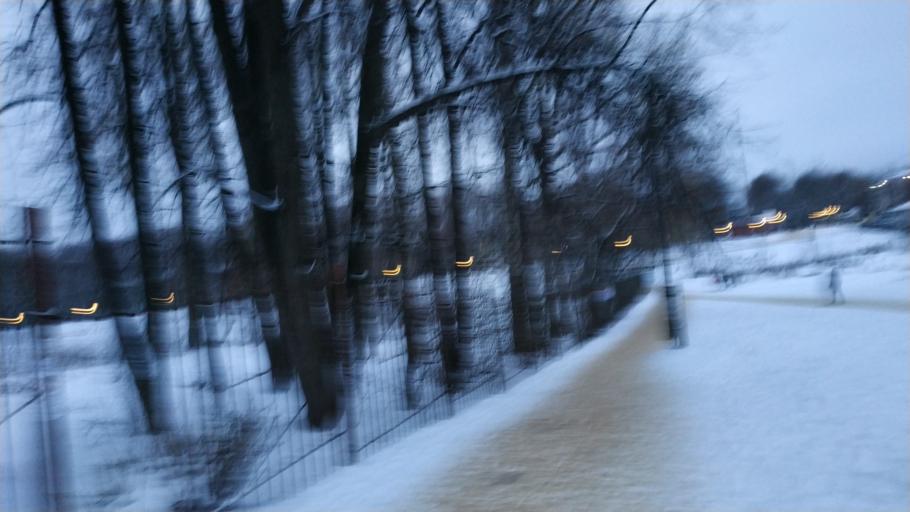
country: RU
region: Moskovskaya
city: Shchelkovo
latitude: 55.9257
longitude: 37.9813
